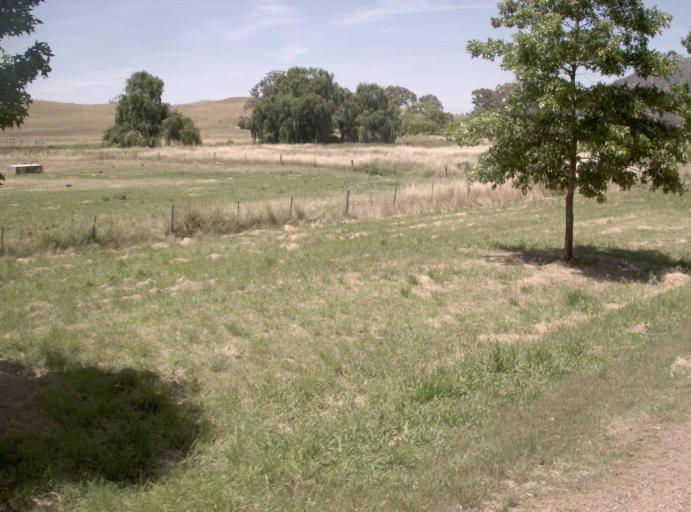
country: AU
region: Victoria
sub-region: East Gippsland
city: Bairnsdale
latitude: -37.2507
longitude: 147.7120
